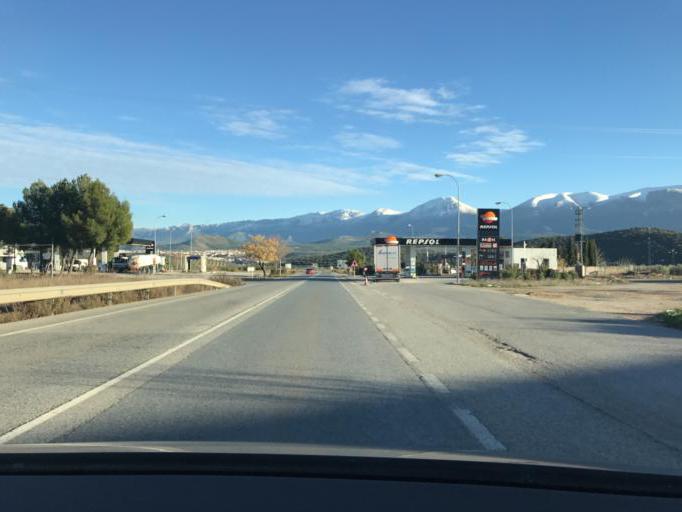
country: ES
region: Andalusia
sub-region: Provincia de Granada
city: Iznalloz
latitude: 37.4014
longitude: -3.5555
